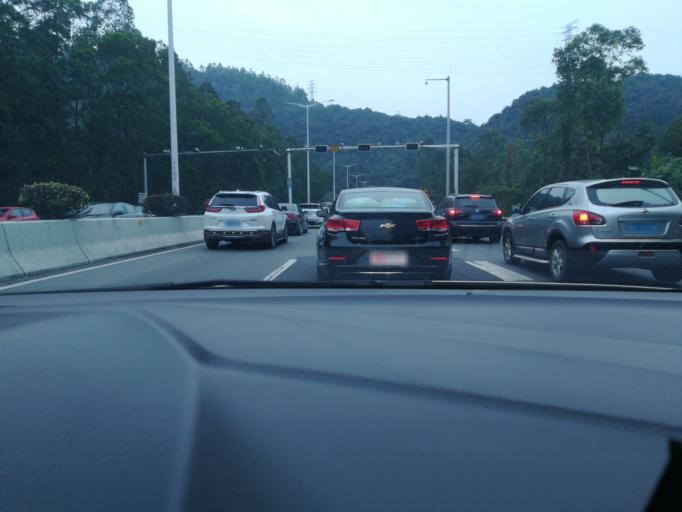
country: CN
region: Guangdong
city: Longdong
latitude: 23.2258
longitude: 113.3564
